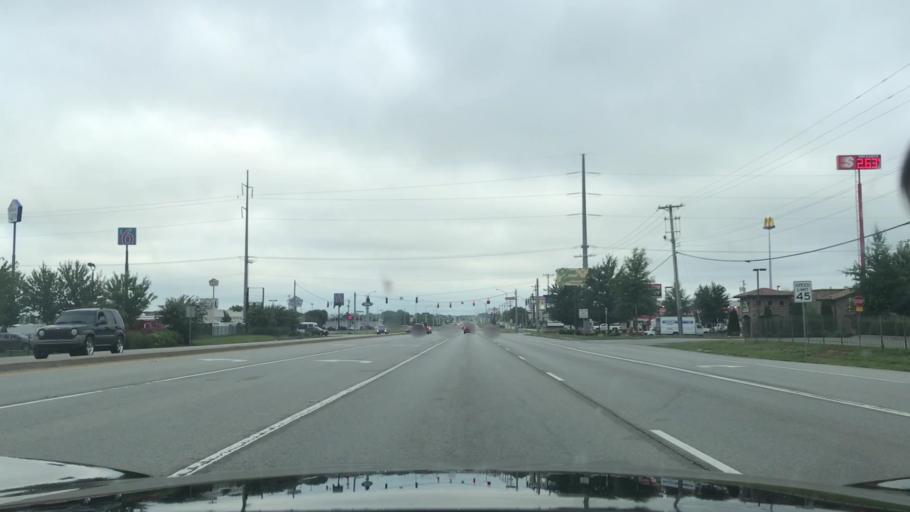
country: US
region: Kentucky
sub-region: Warren County
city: Bowling Green
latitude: 36.9387
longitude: -86.4200
